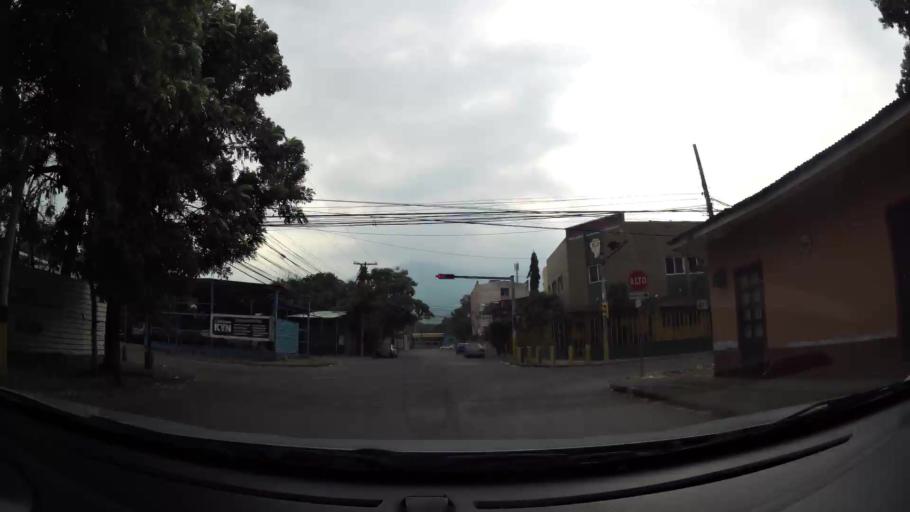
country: HN
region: Cortes
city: San Pedro Sula
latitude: 15.5116
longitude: -88.0292
